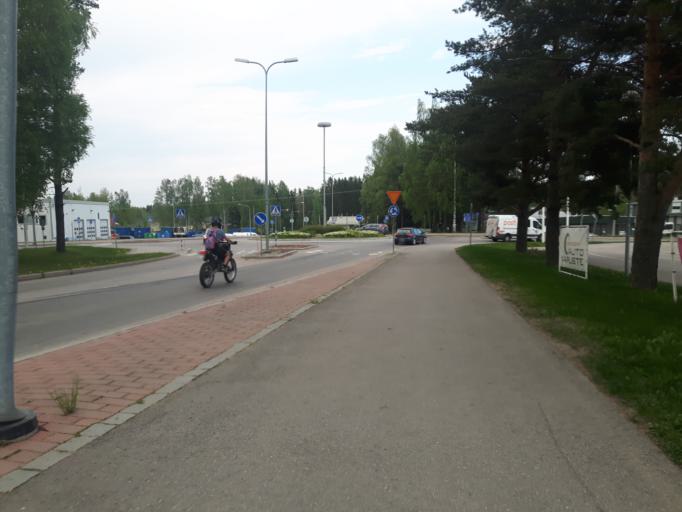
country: FI
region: Uusimaa
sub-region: Porvoo
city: Porvoo
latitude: 60.4003
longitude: 25.6938
